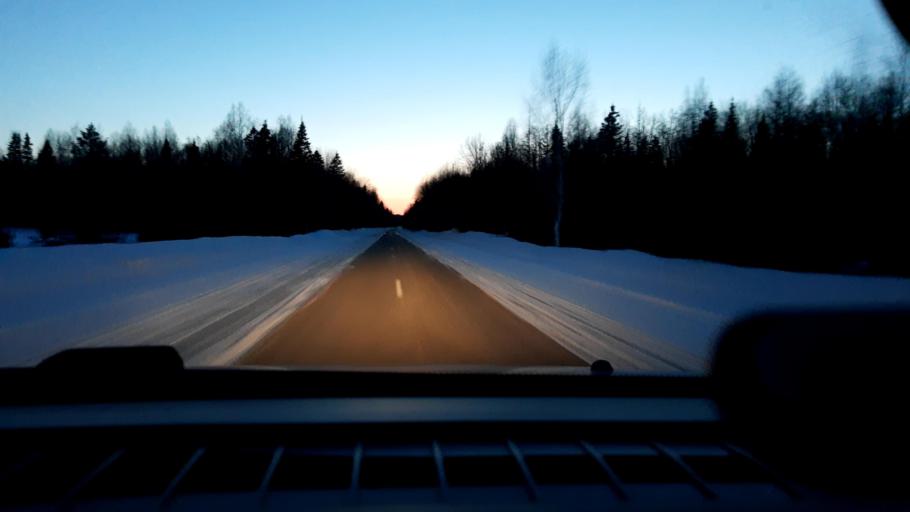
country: RU
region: Nizjnij Novgorod
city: Lyskovo
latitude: 56.1511
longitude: 45.4212
